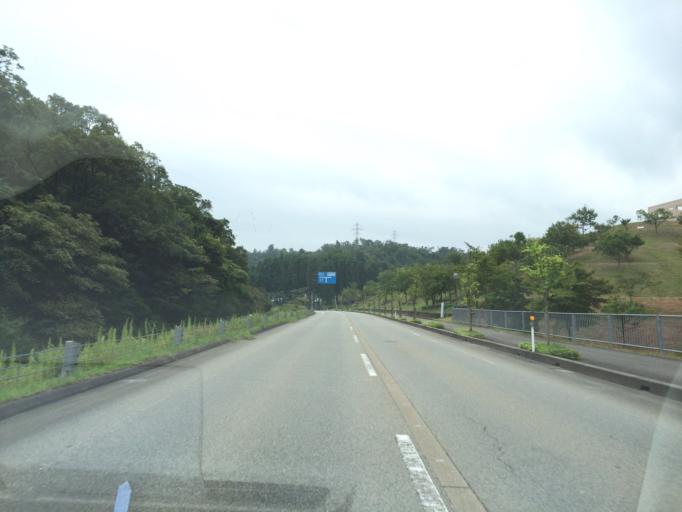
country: JP
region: Hyogo
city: Toyooka
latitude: 35.5283
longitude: 134.8087
